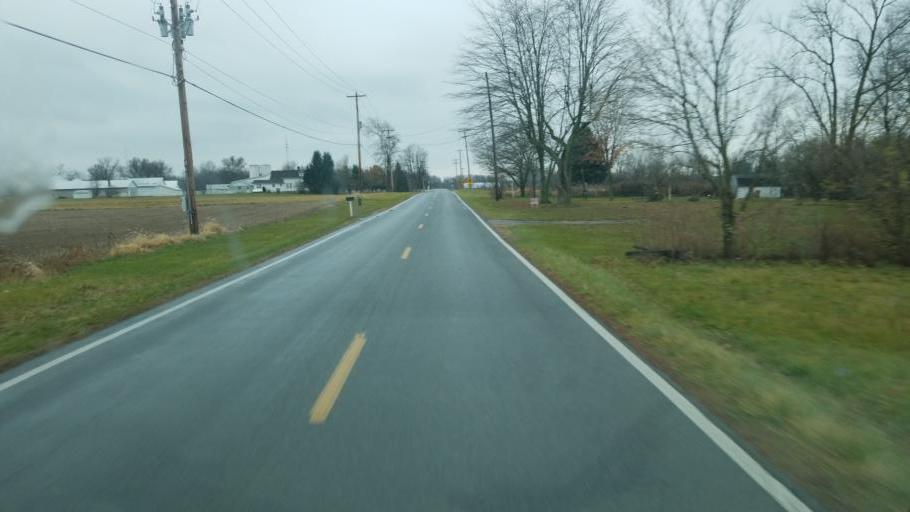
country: US
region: Ohio
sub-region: Delaware County
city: Delaware
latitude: 40.3203
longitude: -83.0481
